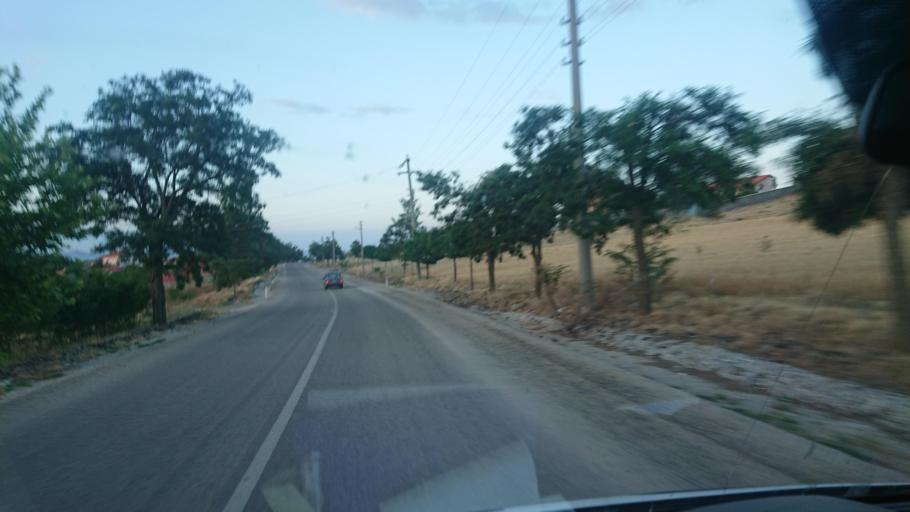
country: TR
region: Aksaray
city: Sariyahsi
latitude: 38.9757
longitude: 33.8353
